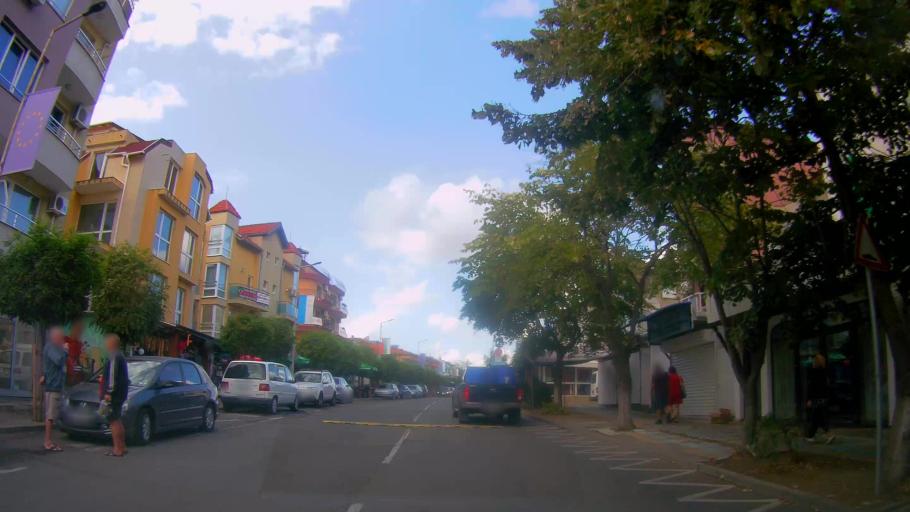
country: BG
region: Burgas
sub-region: Obshtina Primorsko
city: Primorsko
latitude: 42.2671
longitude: 27.7493
